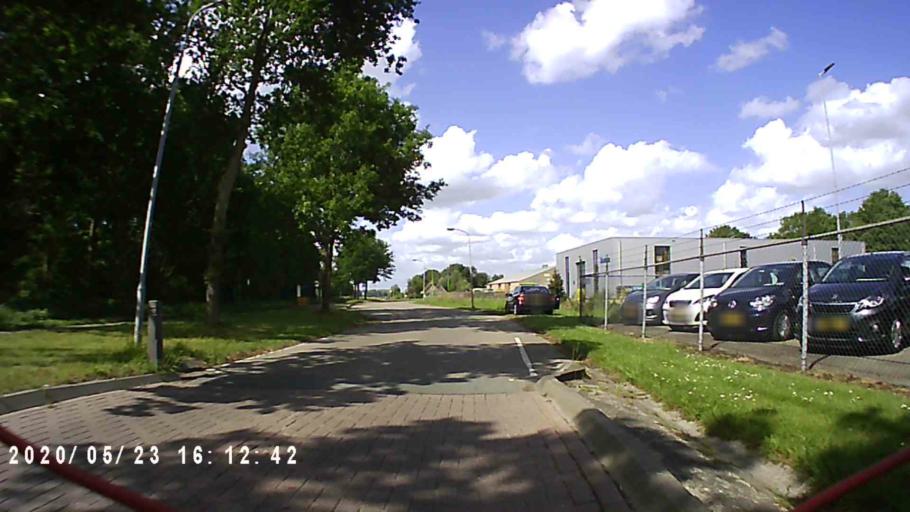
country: NL
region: Groningen
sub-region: Gemeente Appingedam
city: Appingedam
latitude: 53.2499
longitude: 6.8746
